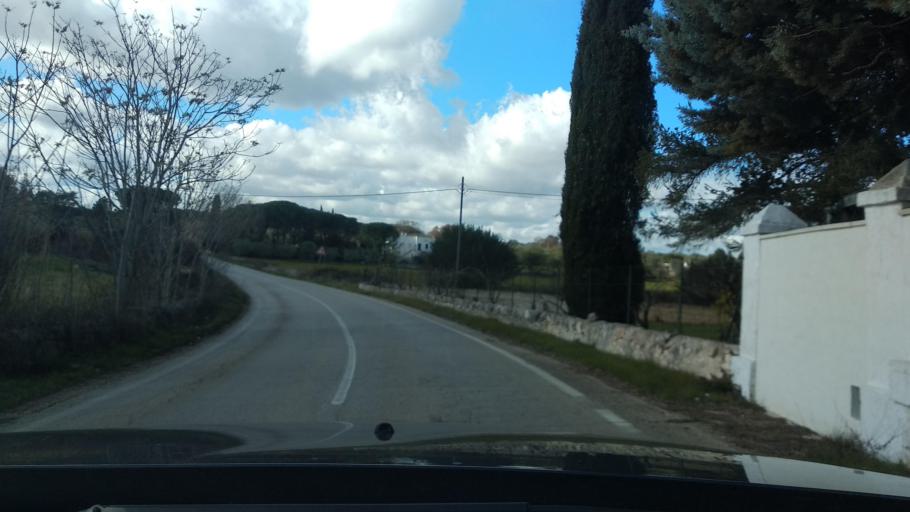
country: IT
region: Apulia
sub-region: Provincia di Brindisi
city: Casalini
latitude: 40.7089
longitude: 17.5198
